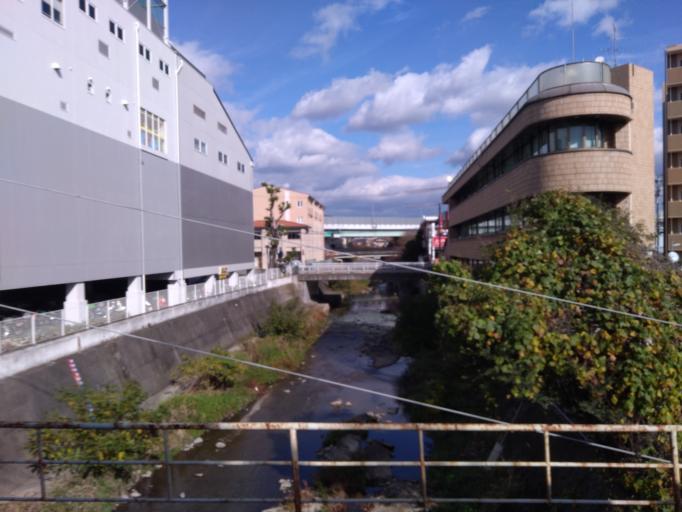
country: JP
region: Osaka
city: Ikeda
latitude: 34.8096
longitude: 135.4445
